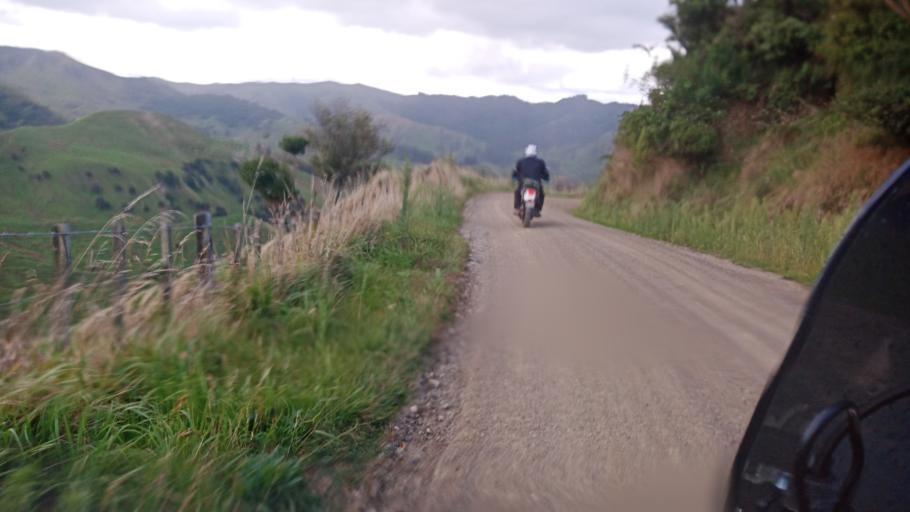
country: NZ
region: Gisborne
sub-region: Gisborne District
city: Gisborne
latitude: -38.4668
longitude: 177.6208
